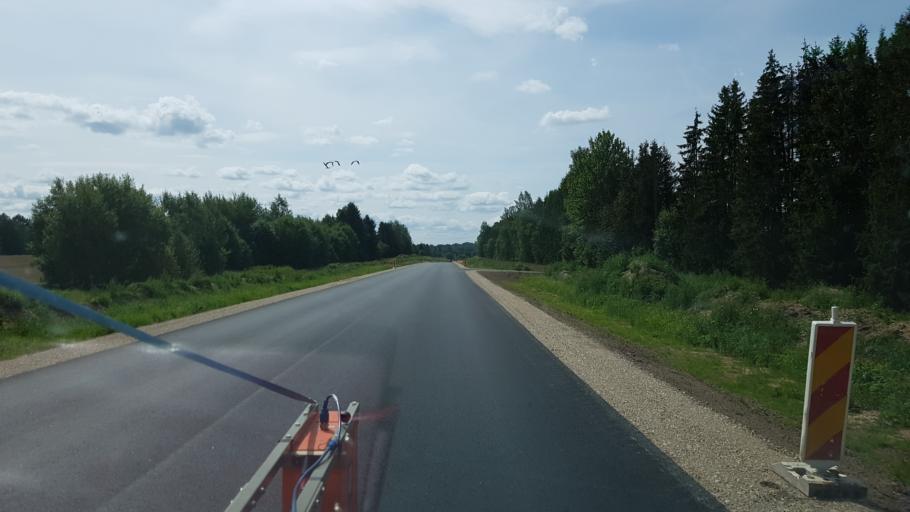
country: LV
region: Aluksnes Rajons
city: Aluksne
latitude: 57.6161
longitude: 27.2660
